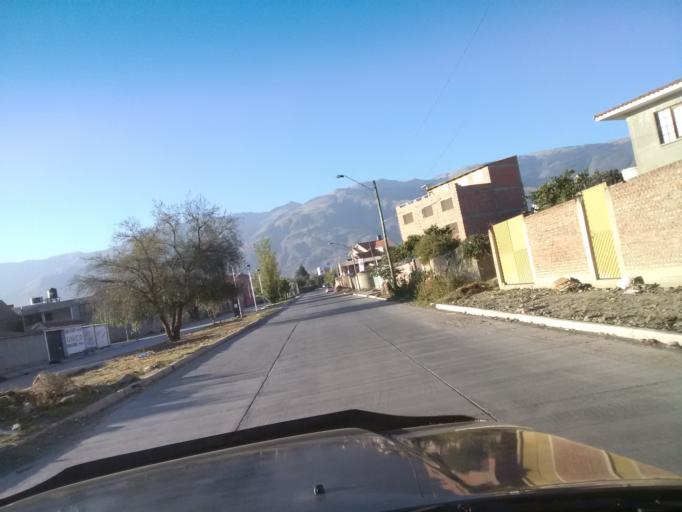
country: BO
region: Cochabamba
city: Cochabamba
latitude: -17.3740
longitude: -66.1919
